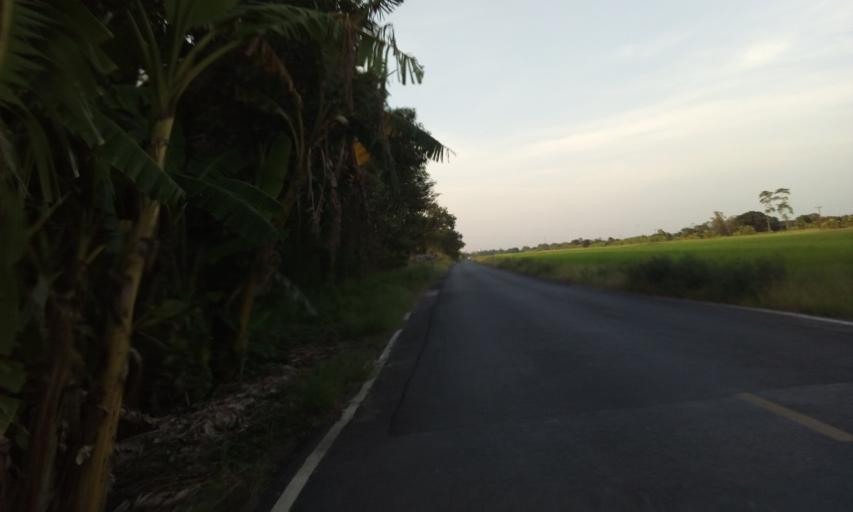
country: TH
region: Pathum Thani
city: Nong Suea
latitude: 14.0516
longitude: 100.8672
